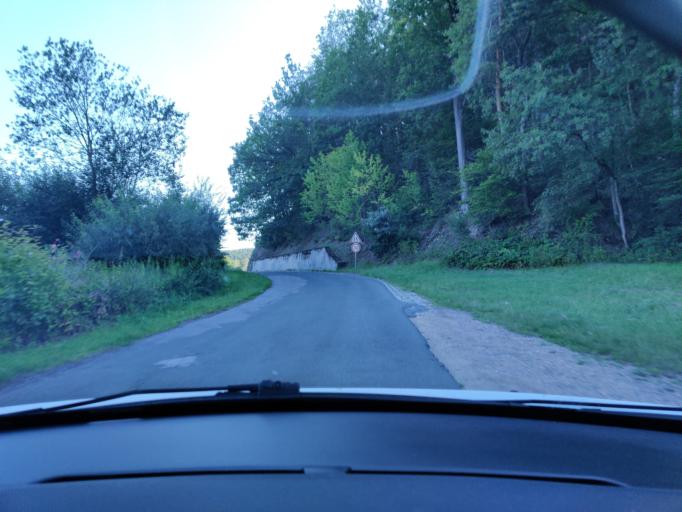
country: DE
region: Bavaria
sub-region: Upper Palatinate
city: Nabburg
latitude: 49.4317
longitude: 12.1684
